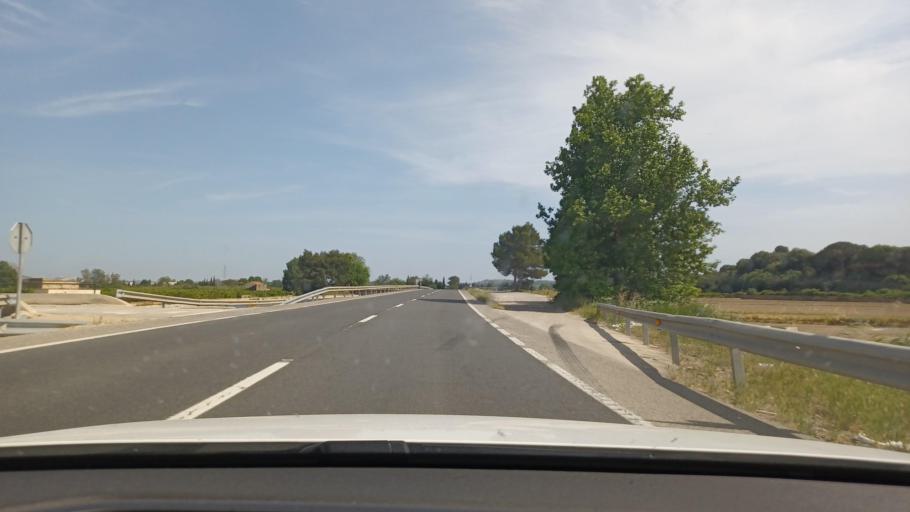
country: ES
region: Catalonia
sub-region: Provincia de Tarragona
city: Tortosa
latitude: 40.7739
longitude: 0.5268
